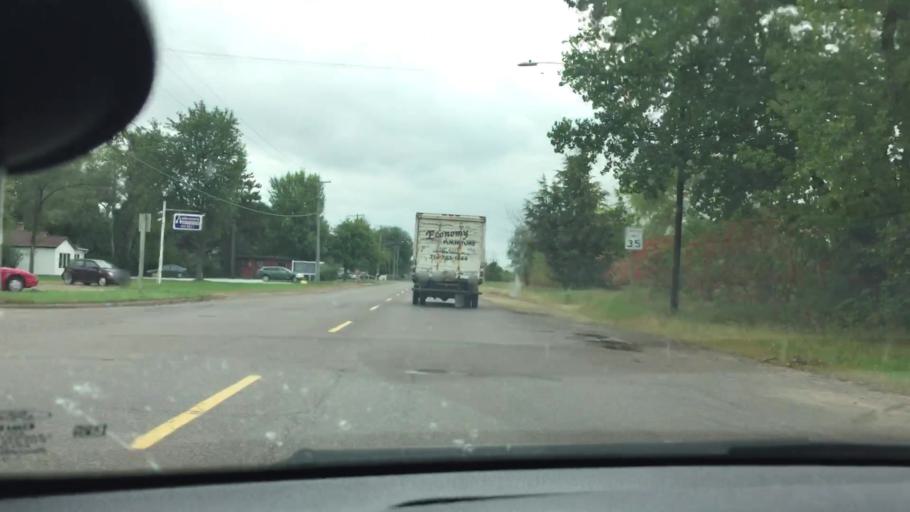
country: US
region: Wisconsin
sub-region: Chippewa County
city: Chippewa Falls
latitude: 44.9188
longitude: -91.3971
